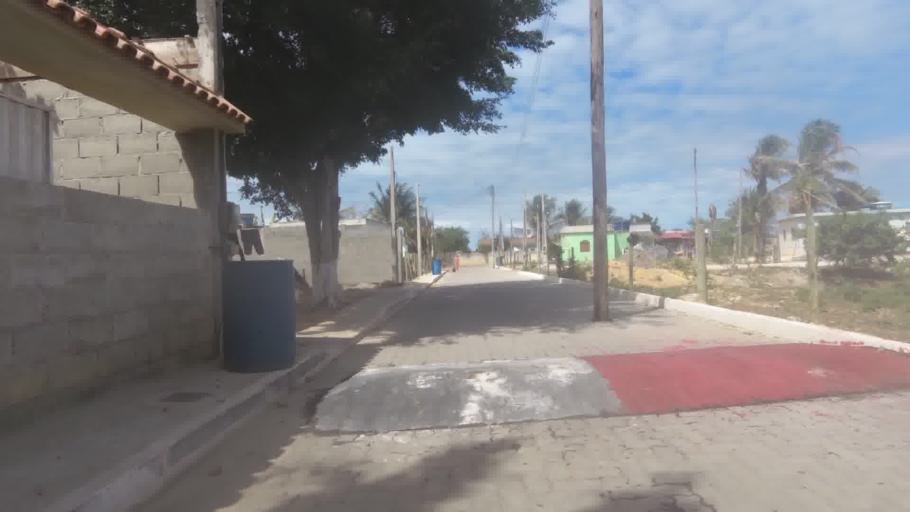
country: BR
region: Espirito Santo
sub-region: Marataizes
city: Marataizes
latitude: -21.2010
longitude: -40.9652
